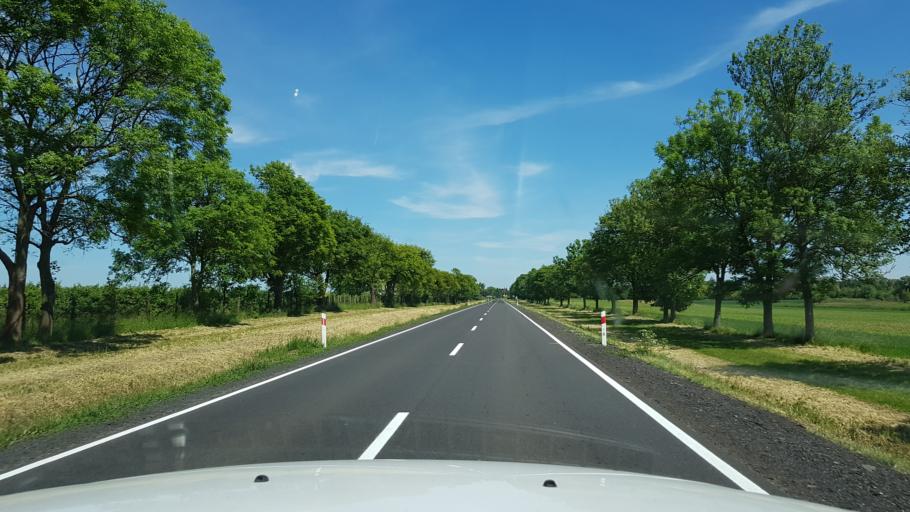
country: PL
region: West Pomeranian Voivodeship
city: Trzcinsko Zdroj
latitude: 52.9617
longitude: 14.5833
